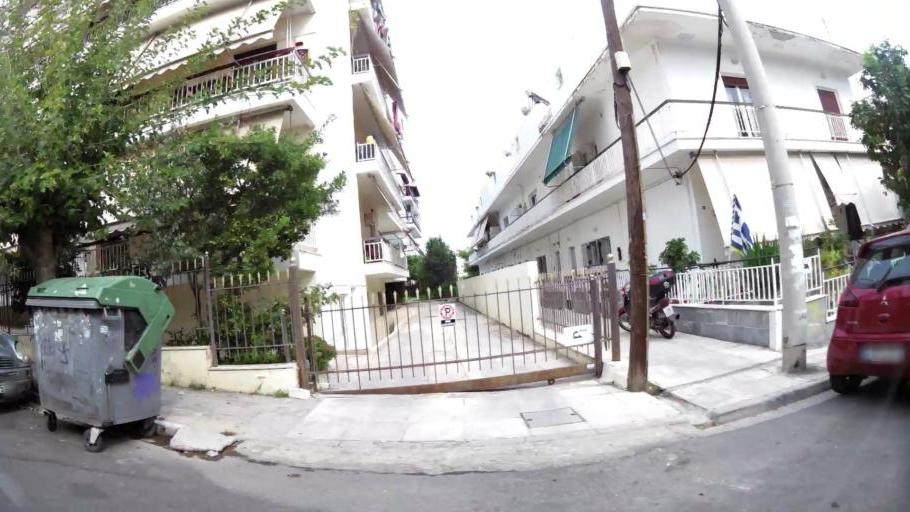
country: GR
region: Attica
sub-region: Nomarchia Athinas
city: Chaidari
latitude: 38.0180
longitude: 23.6513
